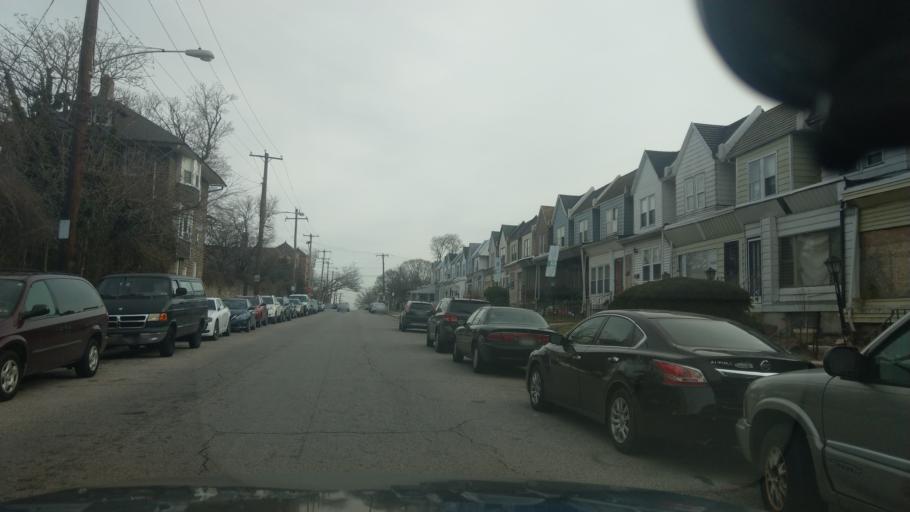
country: US
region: Pennsylvania
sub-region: Montgomery County
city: Wyncote
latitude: 40.0464
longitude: -75.1502
